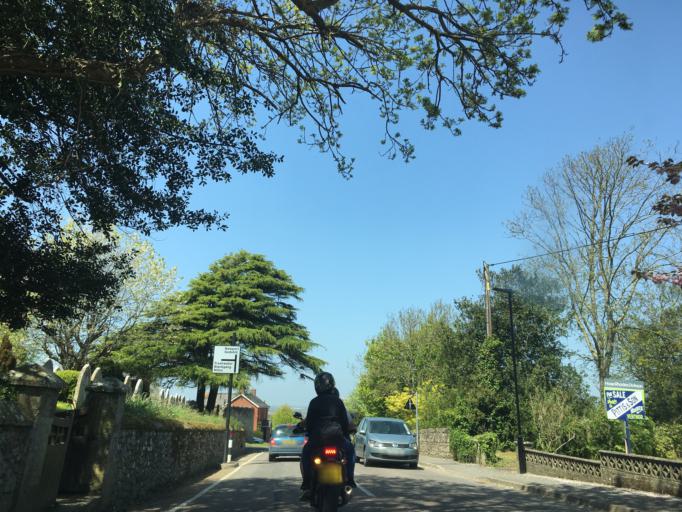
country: GB
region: England
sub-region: Isle of Wight
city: Niton
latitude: 50.5972
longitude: -1.2637
